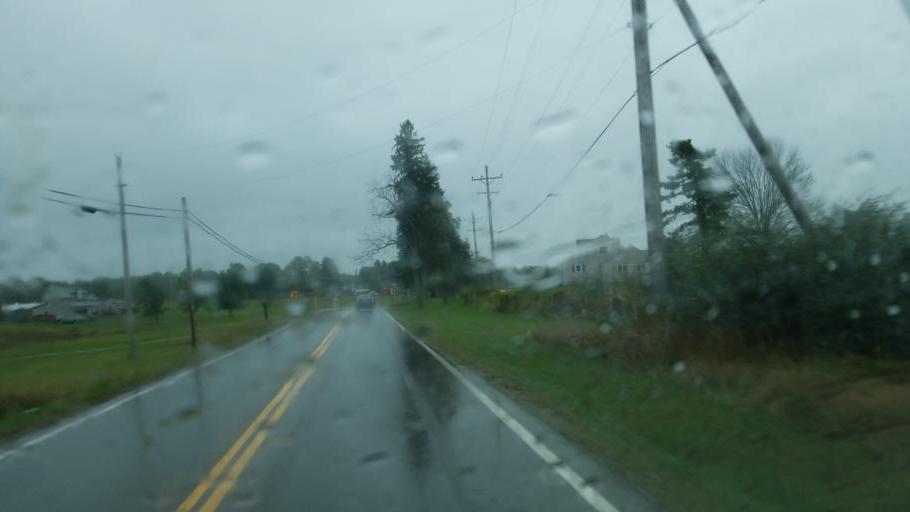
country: US
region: Ohio
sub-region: Richland County
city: Lincoln Heights
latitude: 40.8063
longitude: -82.4898
